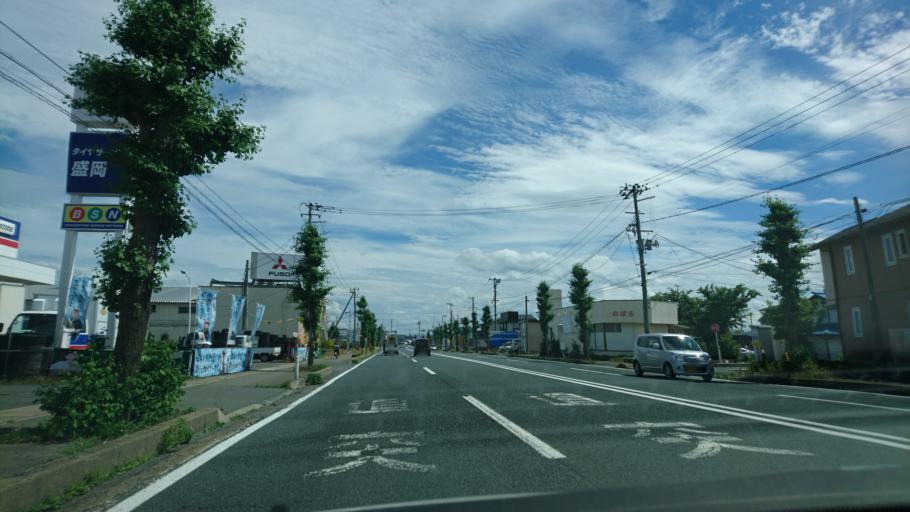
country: JP
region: Iwate
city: Morioka-shi
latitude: 39.6294
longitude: 141.1743
